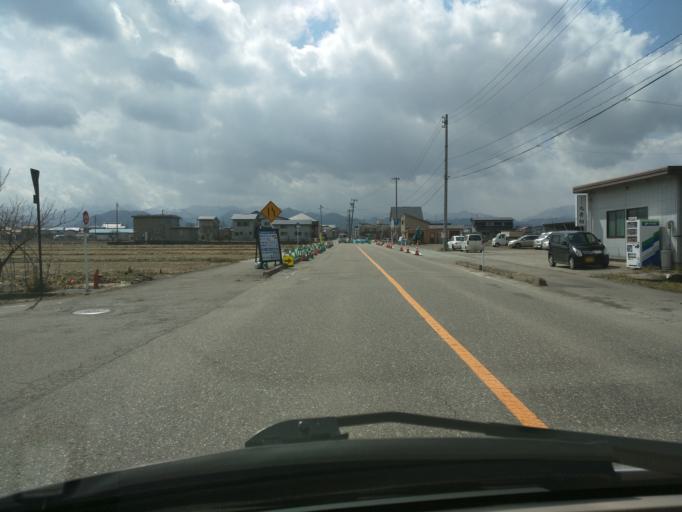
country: JP
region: Fukushima
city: Kitakata
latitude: 37.4733
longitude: 139.8510
